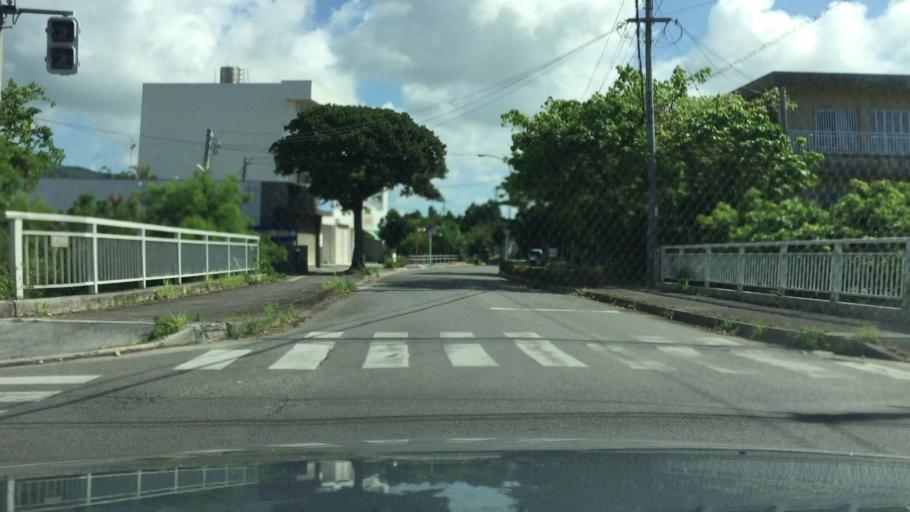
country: JP
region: Okinawa
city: Ishigaki
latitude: 24.3494
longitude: 124.1641
